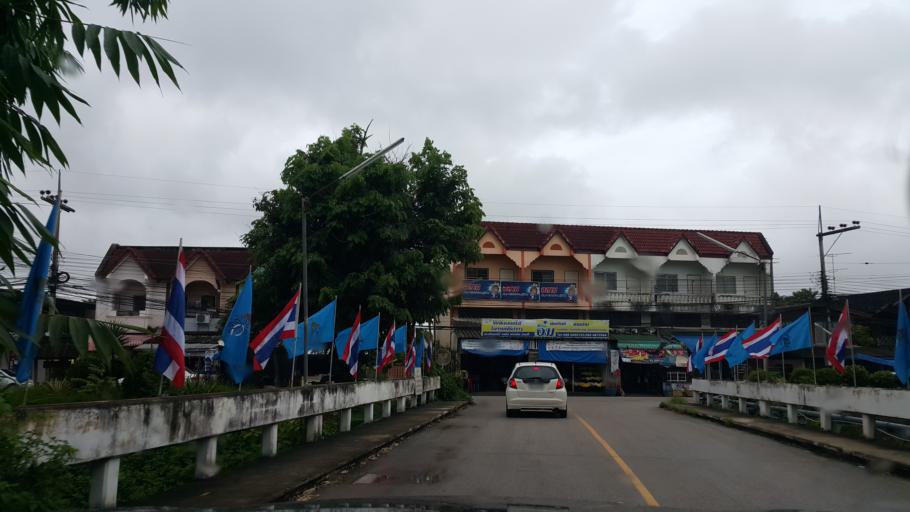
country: TH
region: Phayao
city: Chiang Kham
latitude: 19.5303
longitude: 100.2964
